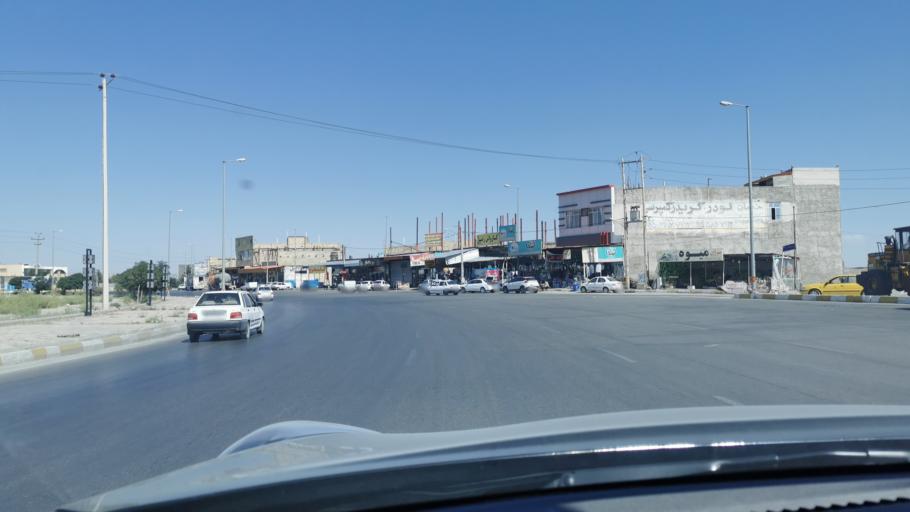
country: IR
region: Razavi Khorasan
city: Chenaran
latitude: 36.6344
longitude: 59.1319
